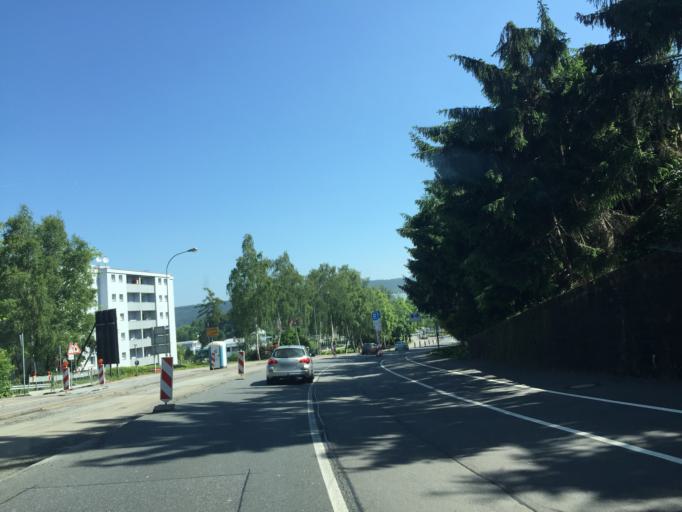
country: DE
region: Hesse
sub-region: Regierungsbezirk Darmstadt
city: Erbach
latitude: 49.6654
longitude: 8.9954
